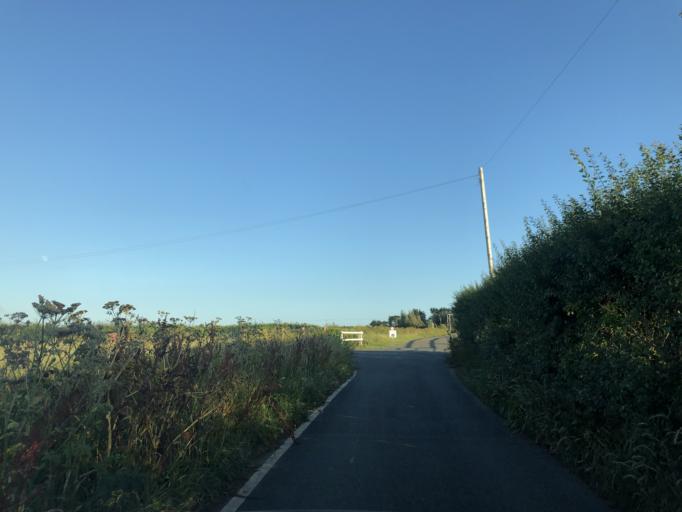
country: GB
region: England
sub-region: Isle of Wight
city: Chale
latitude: 50.6304
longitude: -1.3769
